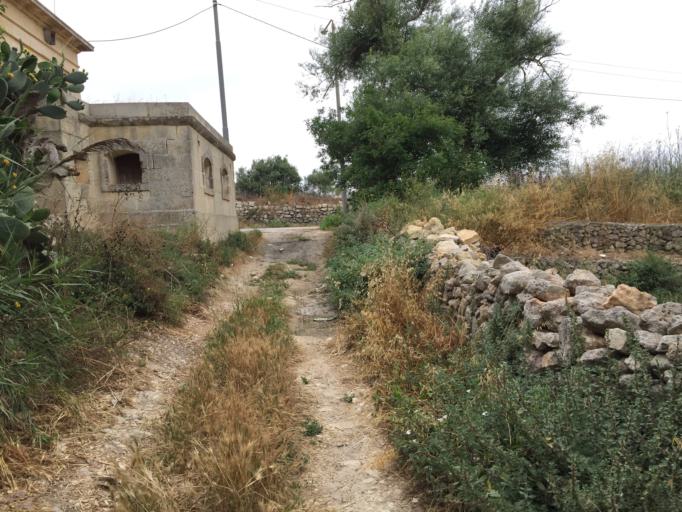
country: MT
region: Ir-Rabat
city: Rabat
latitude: 35.8866
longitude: 14.3803
